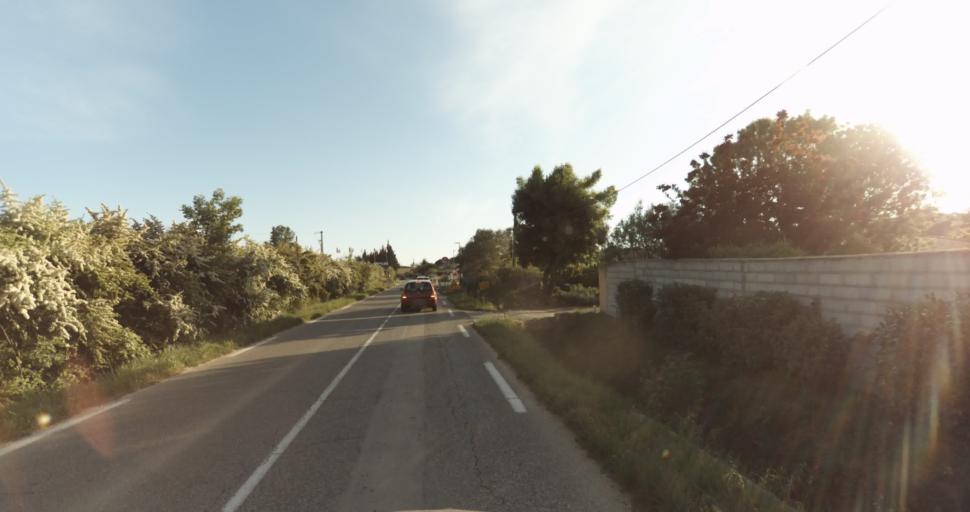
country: FR
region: Provence-Alpes-Cote d'Azur
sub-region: Departement du Var
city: La Crau
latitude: 43.1630
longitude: 6.1011
